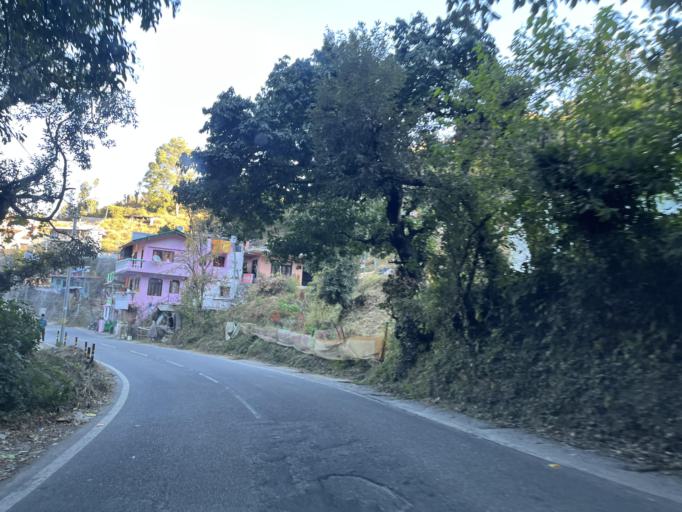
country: IN
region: Uttarakhand
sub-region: Naini Tal
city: Bhowali
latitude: 29.4046
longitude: 79.5153
